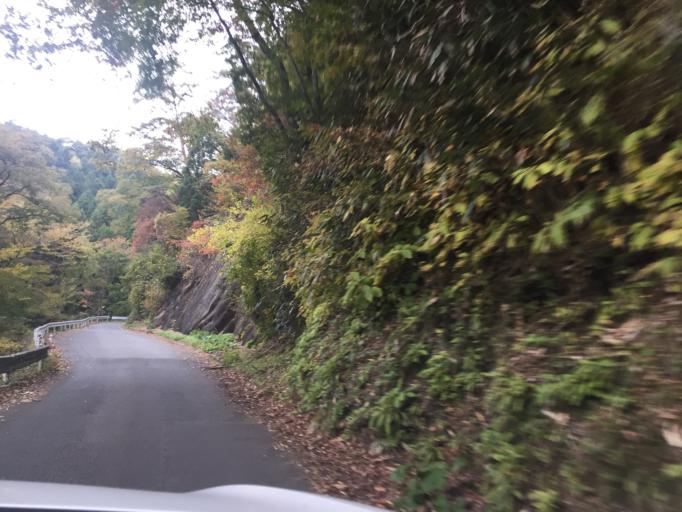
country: JP
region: Fukushima
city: Iwaki
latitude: 37.2055
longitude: 140.7620
